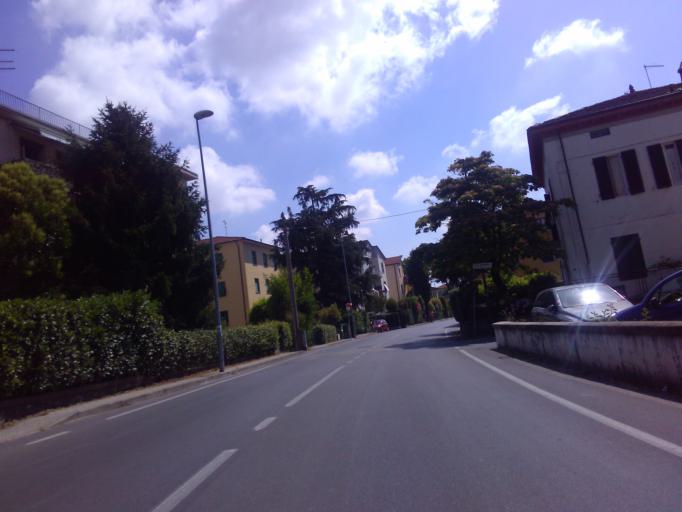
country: IT
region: Tuscany
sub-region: Provincia di Lucca
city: Lucca
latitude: 43.8418
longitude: 10.4866
